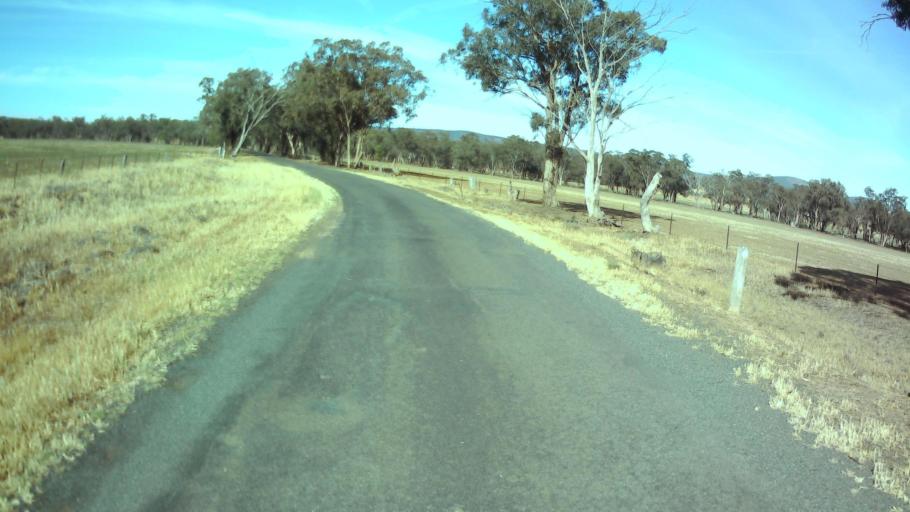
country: AU
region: New South Wales
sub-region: Weddin
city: Grenfell
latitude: -33.9051
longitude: 148.0848
